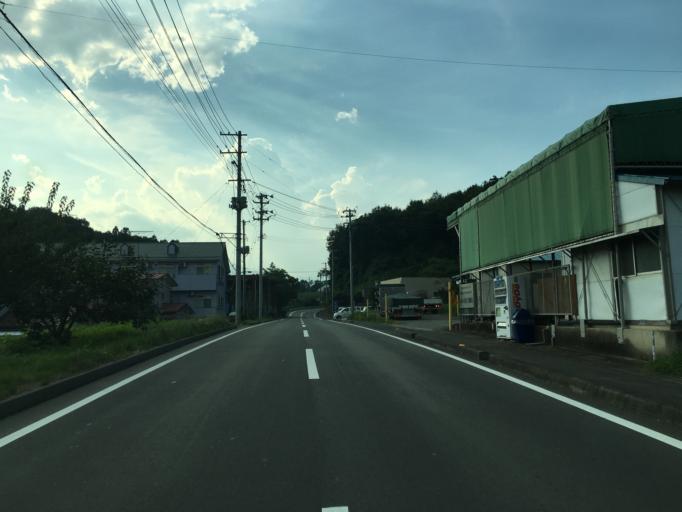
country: JP
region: Fukushima
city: Nihommatsu
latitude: 37.5725
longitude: 140.4330
